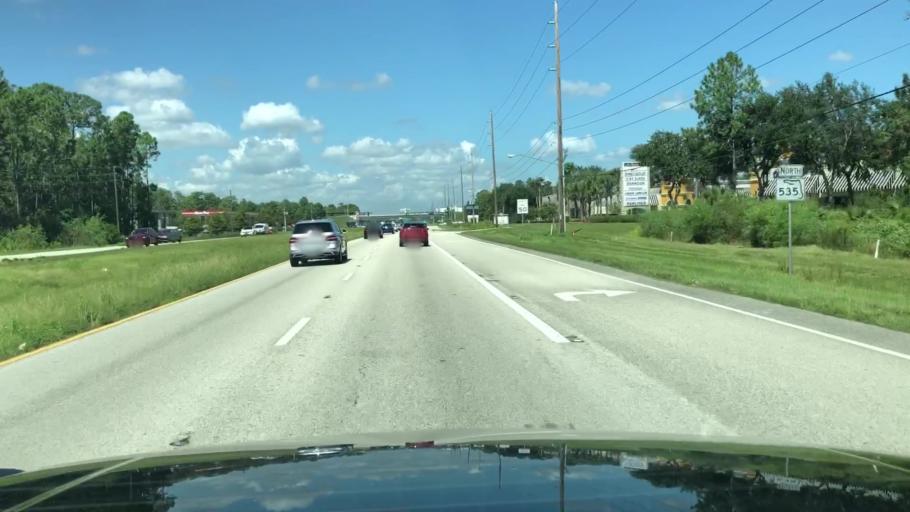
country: US
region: Florida
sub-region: Osceola County
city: Celebration
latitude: 28.3475
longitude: -81.4879
